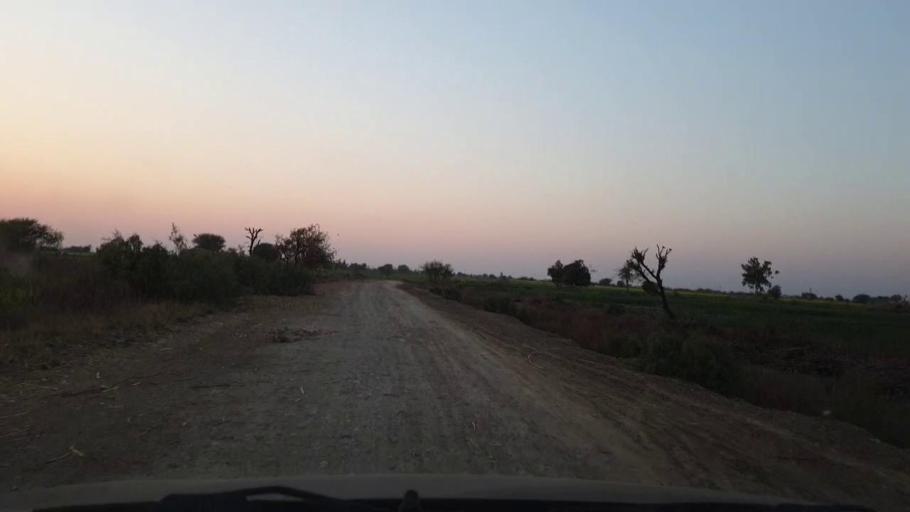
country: PK
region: Sindh
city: Jhol
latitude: 25.9390
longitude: 68.9557
